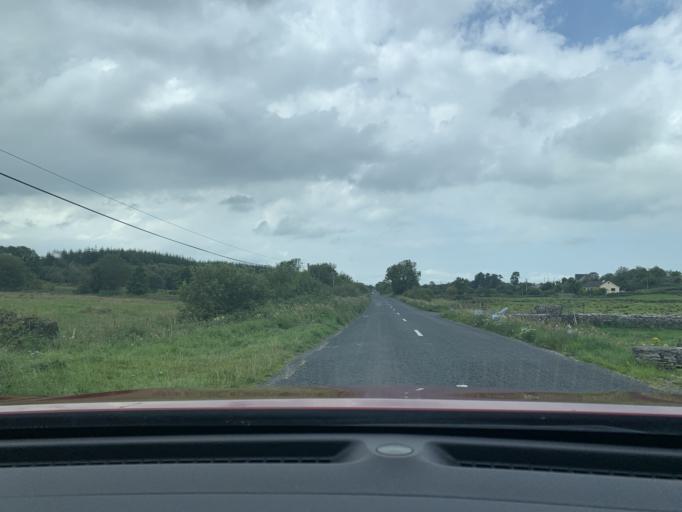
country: IE
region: Connaught
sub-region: Maigh Eo
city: Kiltamagh
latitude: 53.8532
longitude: -8.9387
